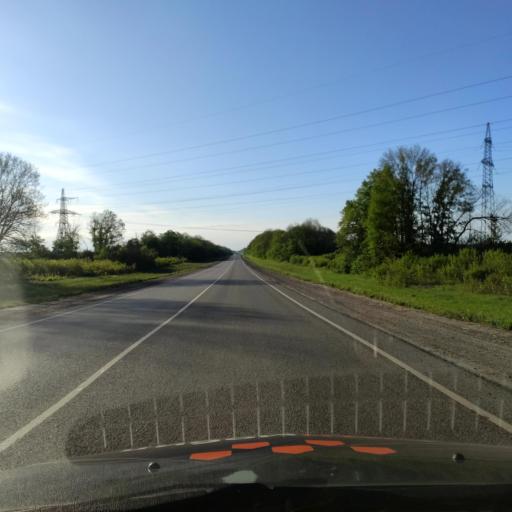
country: RU
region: Lipetsk
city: Yelets
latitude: 52.5778
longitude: 38.6426
